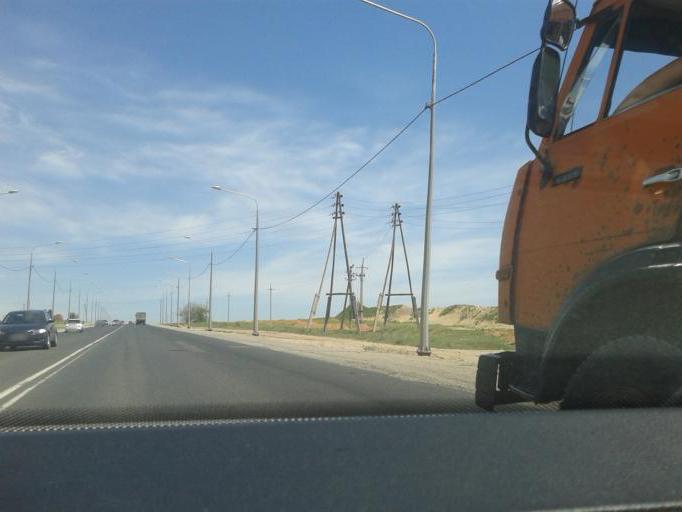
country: RU
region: Volgograd
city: Vodstroy
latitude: 48.8108
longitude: 44.5238
